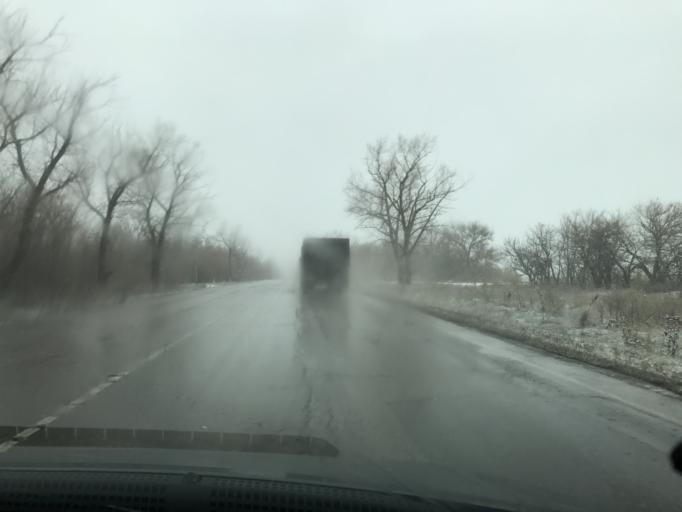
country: RU
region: Rostov
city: Bataysk
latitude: 47.0387
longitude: 39.8620
